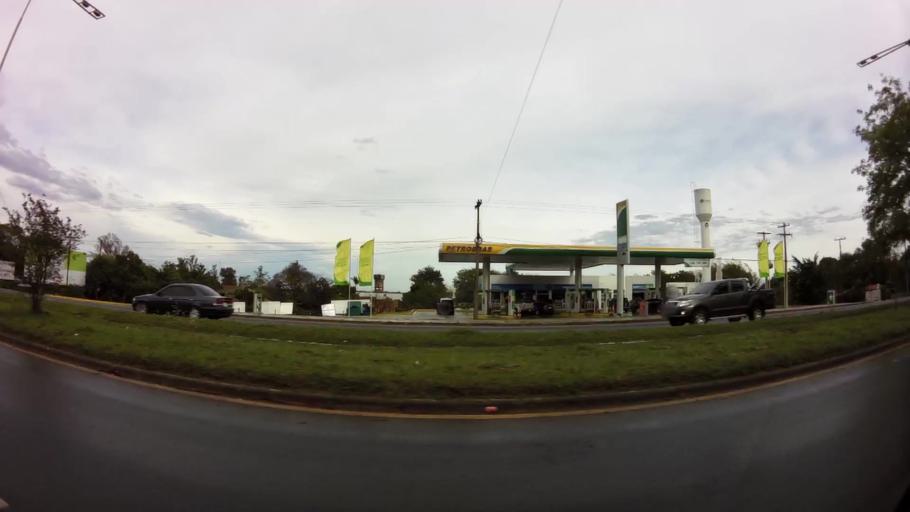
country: PY
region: Central
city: Fernando de la Mora
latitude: -25.2547
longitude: -57.5137
